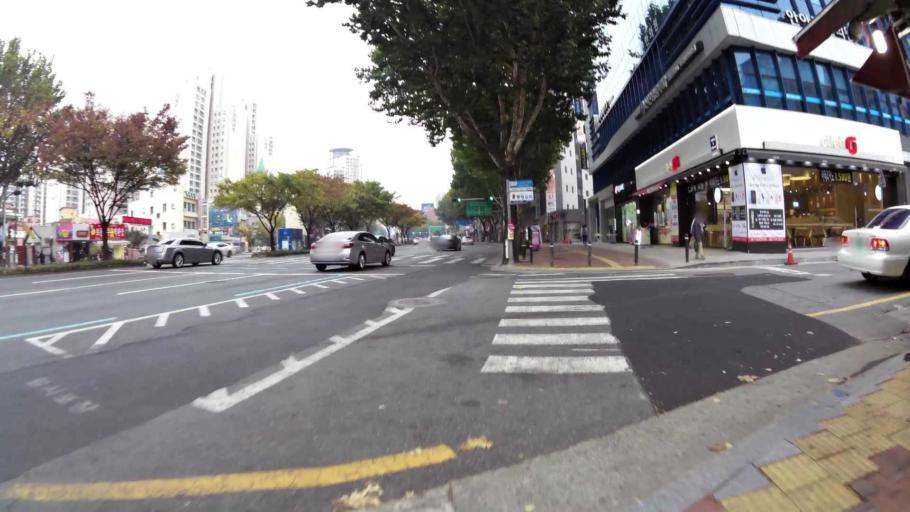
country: KR
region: Daegu
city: Daegu
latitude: 35.8600
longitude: 128.6113
